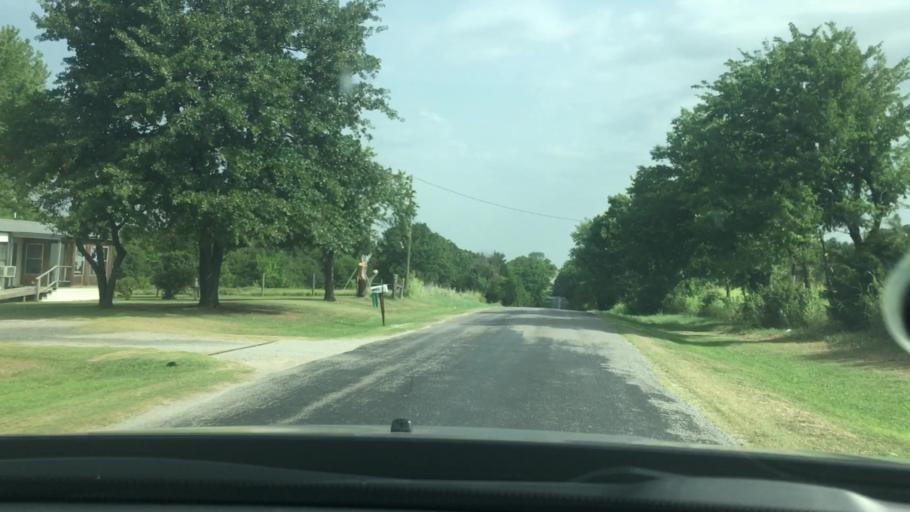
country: US
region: Oklahoma
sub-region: Garvin County
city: Pauls Valley
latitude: 34.8079
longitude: -97.1955
